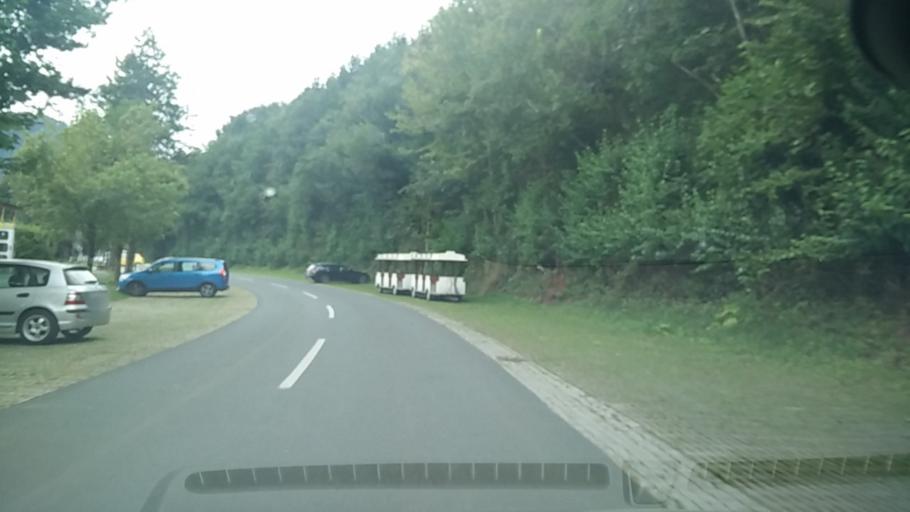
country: AT
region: Carinthia
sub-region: Politischer Bezirk Volkermarkt
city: Sittersdorf
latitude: 46.6011
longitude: 14.5740
